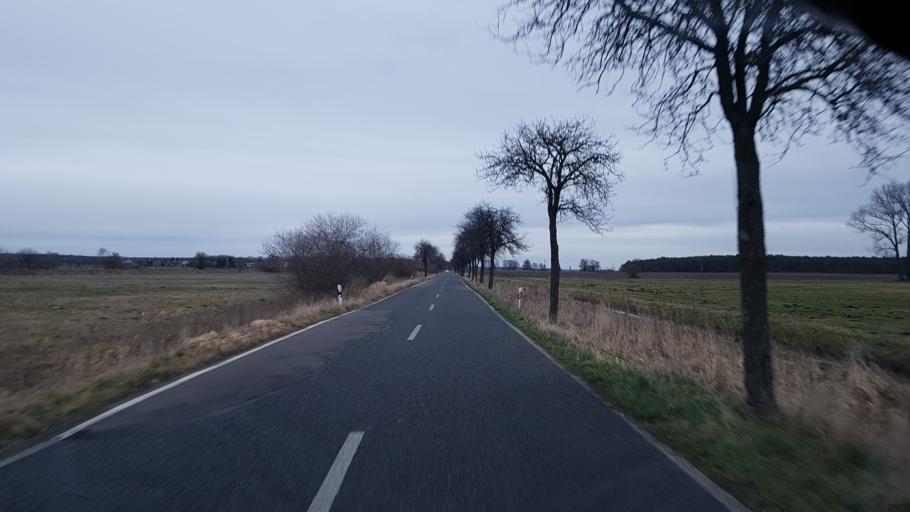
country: DE
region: Brandenburg
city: Schlieben
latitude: 51.7168
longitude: 13.3010
